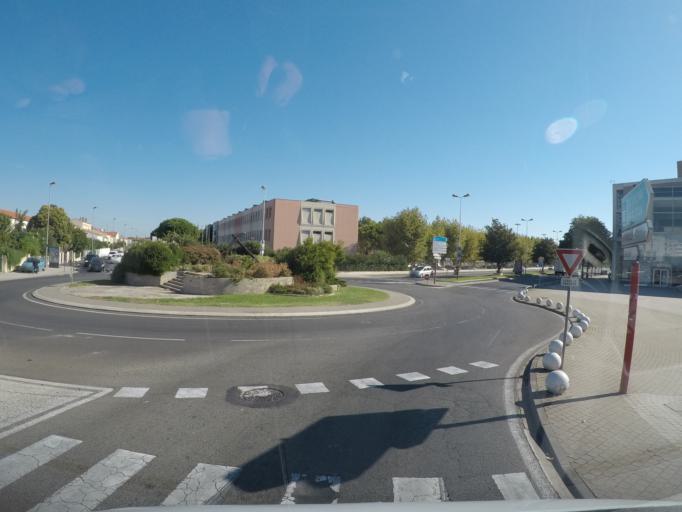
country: FR
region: Languedoc-Roussillon
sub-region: Departement de l'Aude
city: Narbonne
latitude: 43.1802
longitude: 3.0137
